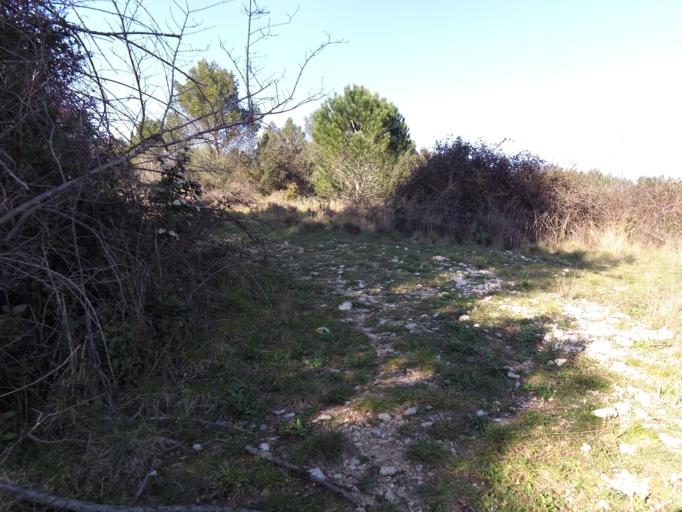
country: FR
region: Languedoc-Roussillon
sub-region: Departement du Gard
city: Congenies
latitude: 43.7601
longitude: 4.1698
